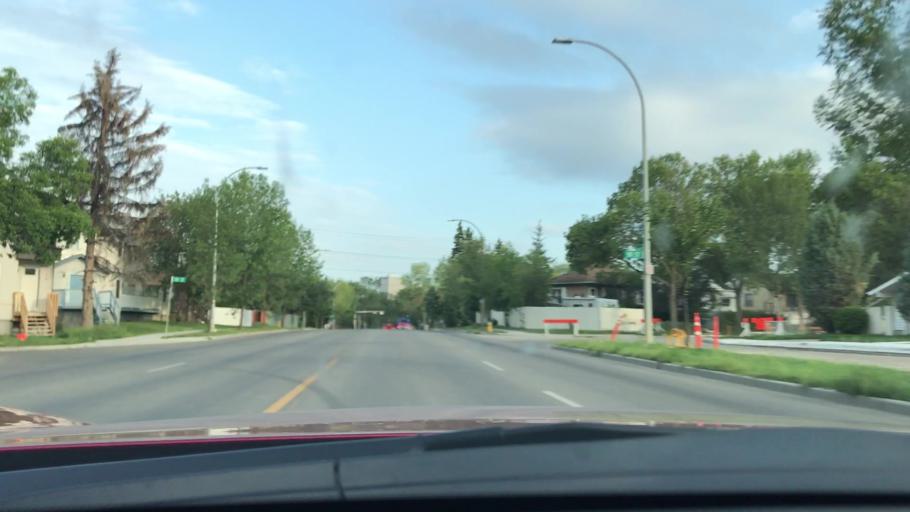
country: CA
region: Alberta
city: Edmonton
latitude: 53.5286
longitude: -113.4650
